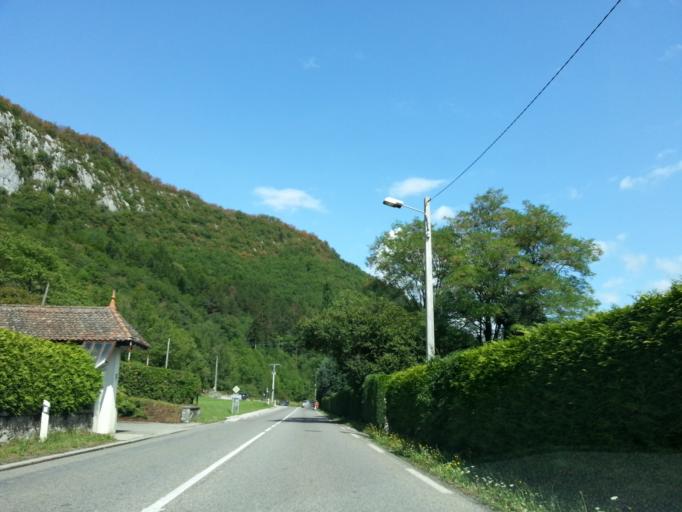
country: FR
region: Rhone-Alpes
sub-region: Departement de la Haute-Savoie
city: Talloires
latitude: 45.8185
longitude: 6.2076
